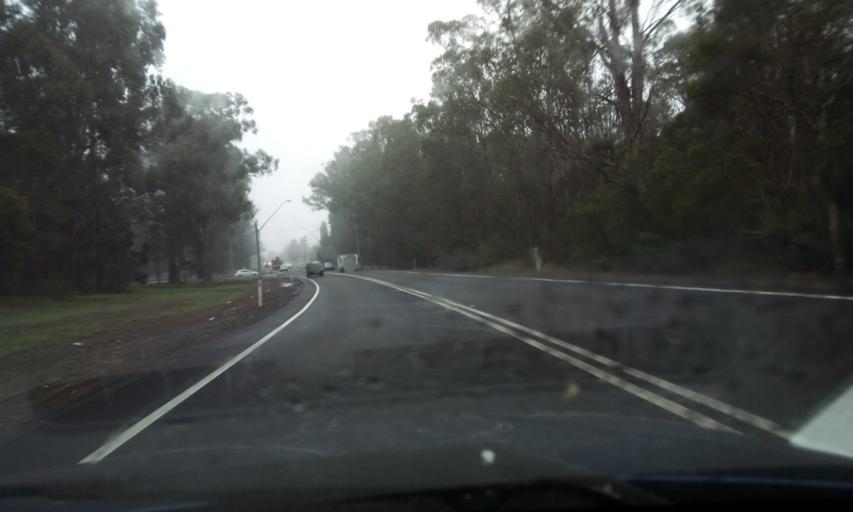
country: AU
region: New South Wales
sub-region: Penrith Municipality
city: Werrington Downs
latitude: -33.7069
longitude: 150.7235
